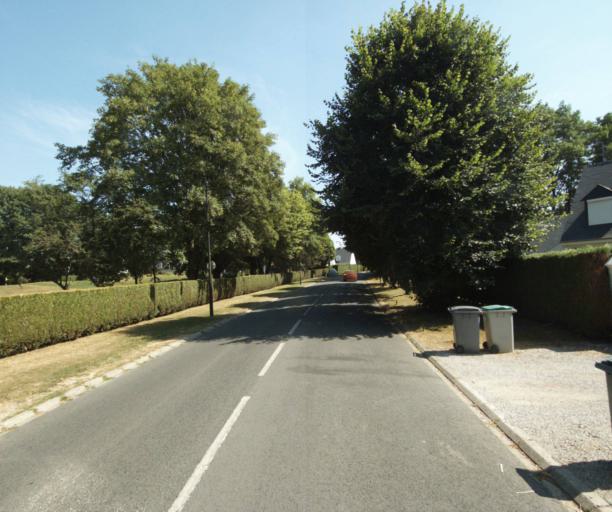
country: FR
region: Nord-Pas-de-Calais
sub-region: Departement du Nord
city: Bondues
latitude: 50.7056
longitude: 3.0824
